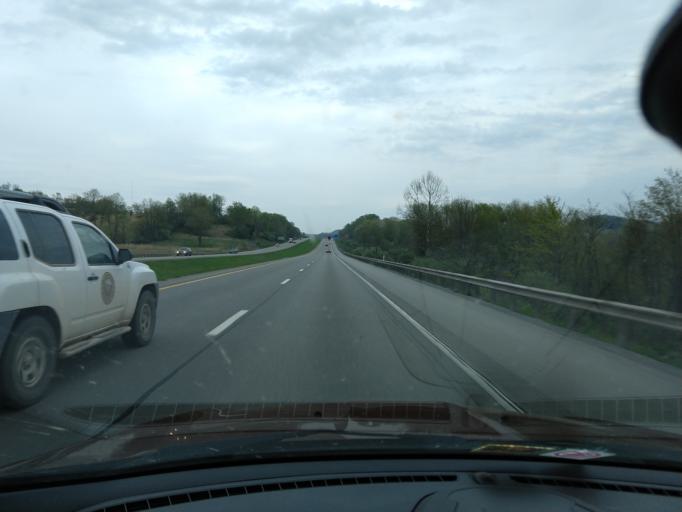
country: US
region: West Virginia
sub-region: Lewis County
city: Weston
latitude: 39.0777
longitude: -80.4028
